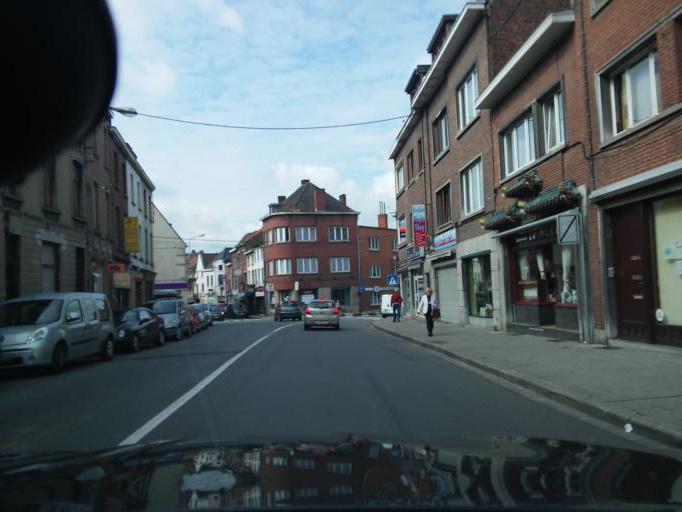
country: BE
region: Wallonia
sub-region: Province du Hainaut
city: Enghien
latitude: 50.6949
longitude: 4.0427
